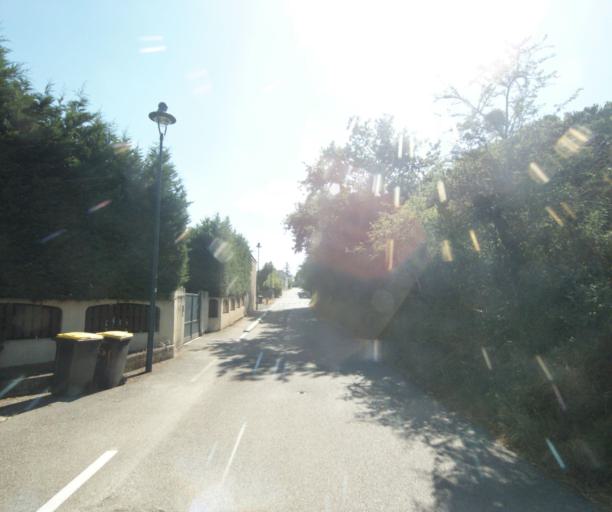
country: FR
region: Rhone-Alpes
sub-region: Departement du Rhone
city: La Tour-de-Salvagny
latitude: 45.8295
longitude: 4.7032
